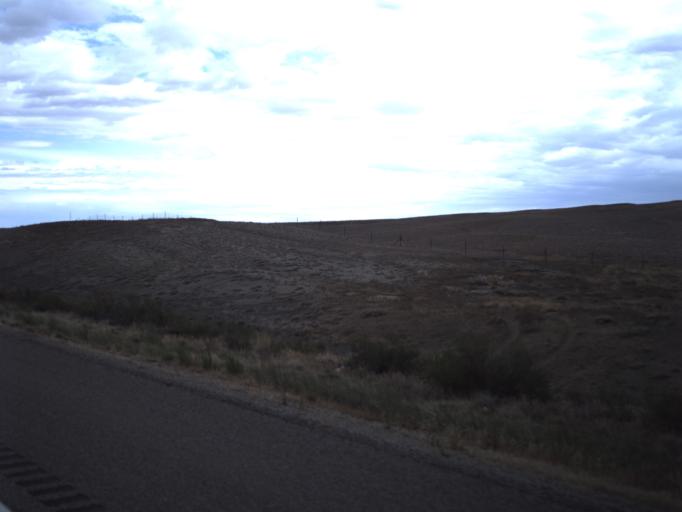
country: US
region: Utah
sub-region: Grand County
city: Moab
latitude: 38.9608
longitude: -110.0651
